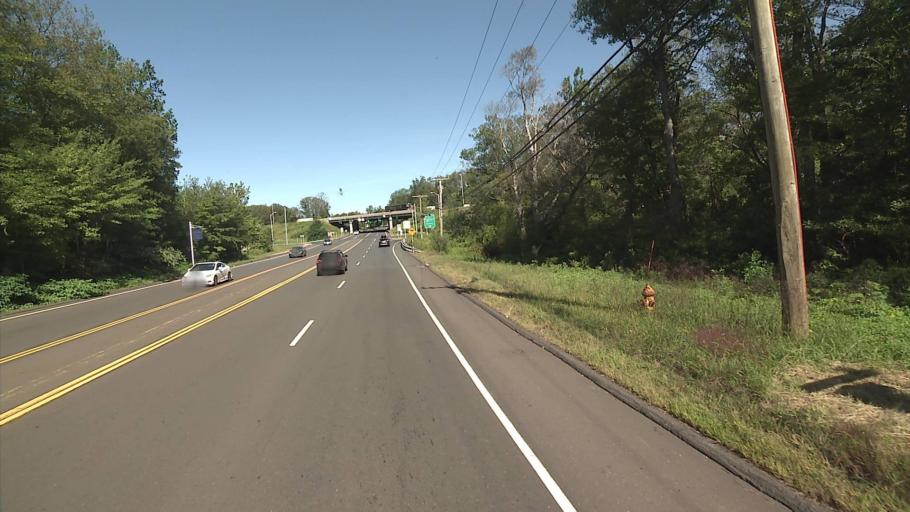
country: US
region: Connecticut
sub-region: New Haven County
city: Prospect
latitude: 41.5402
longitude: -72.9493
